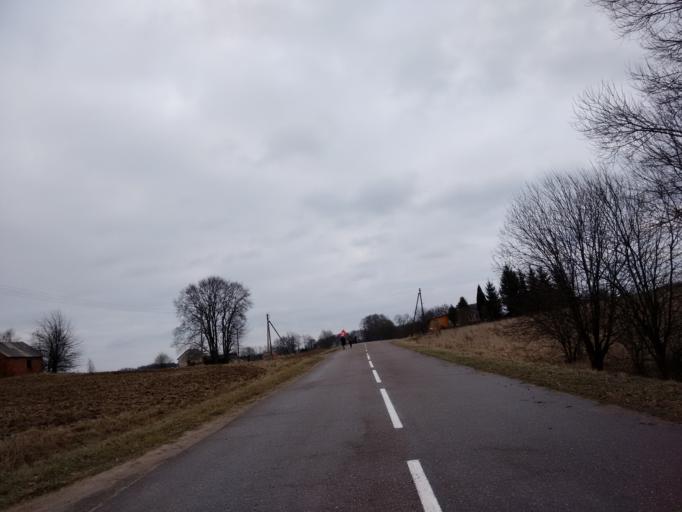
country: LT
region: Alytaus apskritis
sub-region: Alytus
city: Alytus
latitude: 54.2446
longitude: 23.9025
